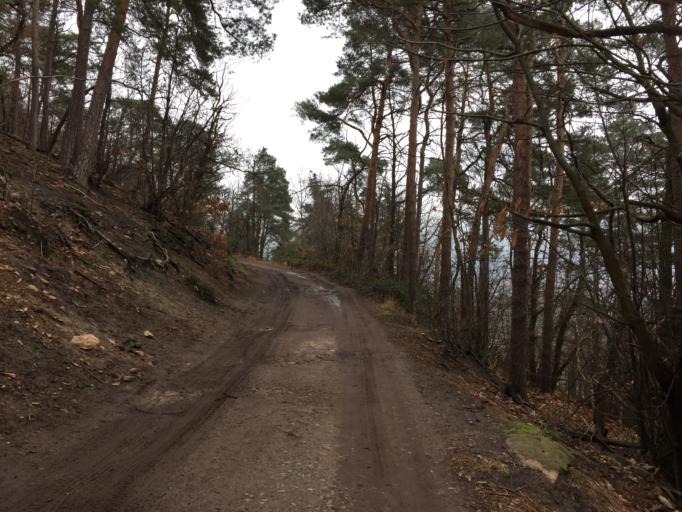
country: DE
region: Rheinland-Pfalz
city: Sankt Martin
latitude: 49.3180
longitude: 8.1097
